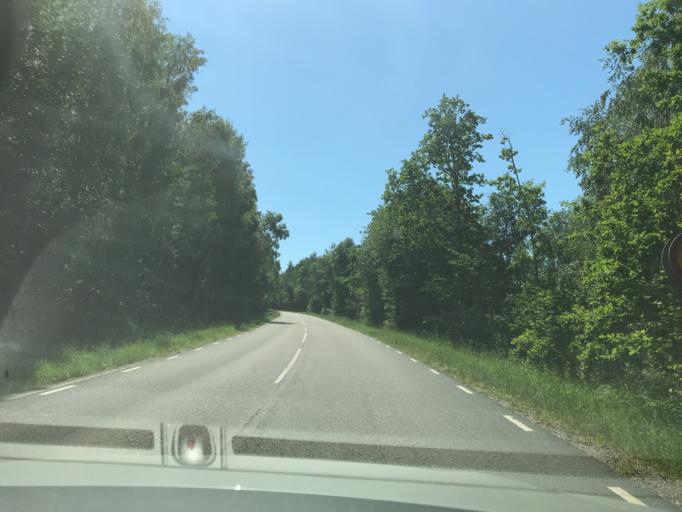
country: SE
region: Vaestra Goetaland
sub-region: Gotene Kommun
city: Goetene
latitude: 58.6219
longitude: 13.4073
